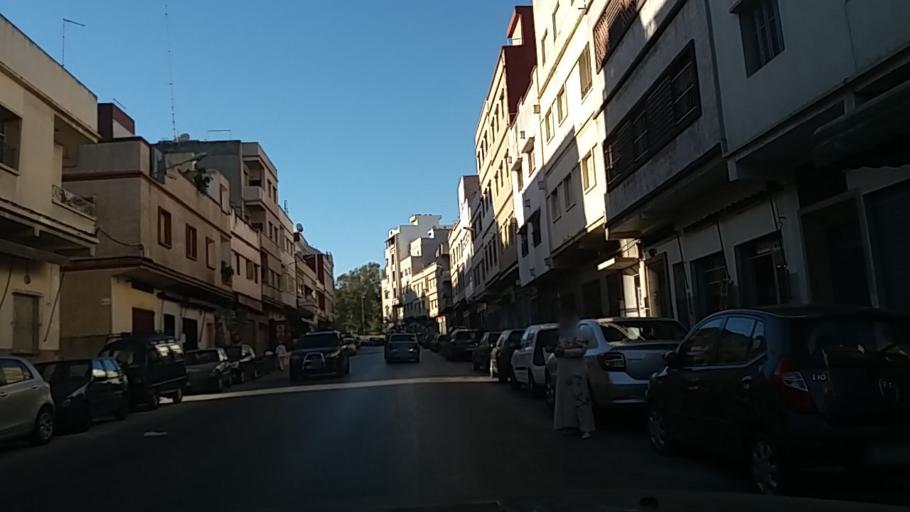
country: MA
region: Tanger-Tetouan
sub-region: Tanger-Assilah
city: Tangier
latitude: 35.7734
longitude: -5.8220
